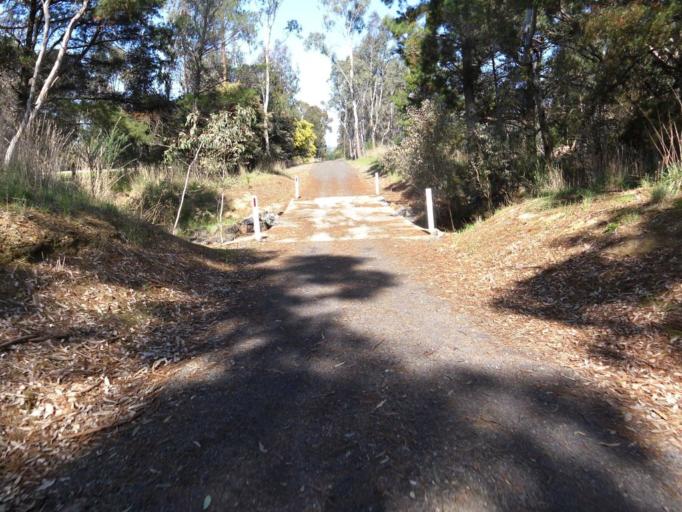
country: AU
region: Victoria
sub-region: Murrindindi
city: Alexandra
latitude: -37.0008
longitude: 145.7457
